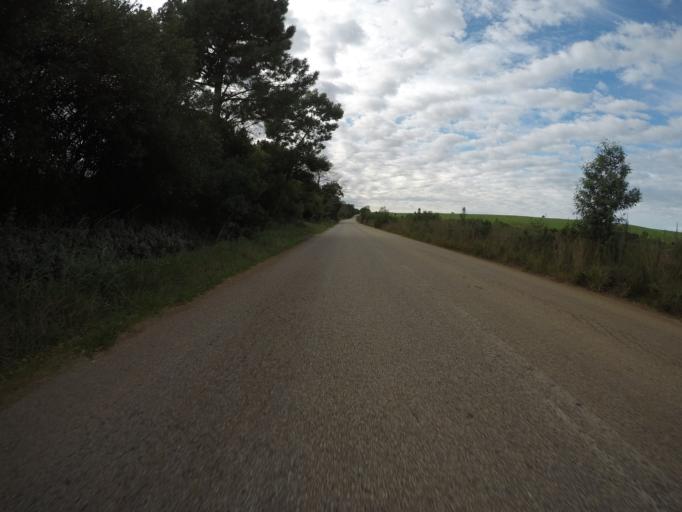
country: ZA
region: Eastern Cape
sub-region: Cacadu District Municipality
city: Kareedouw
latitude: -34.0058
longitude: 24.2435
